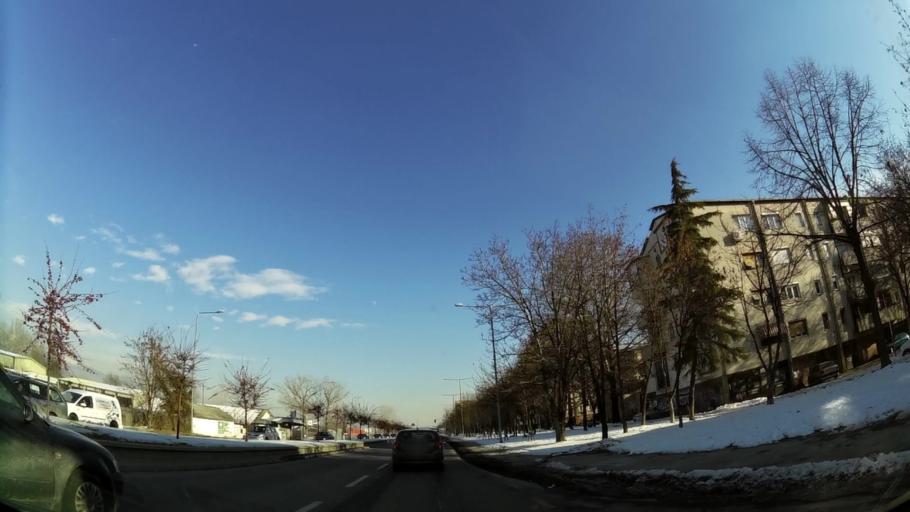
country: MK
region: Karpos
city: Skopje
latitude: 42.0075
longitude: 21.3947
